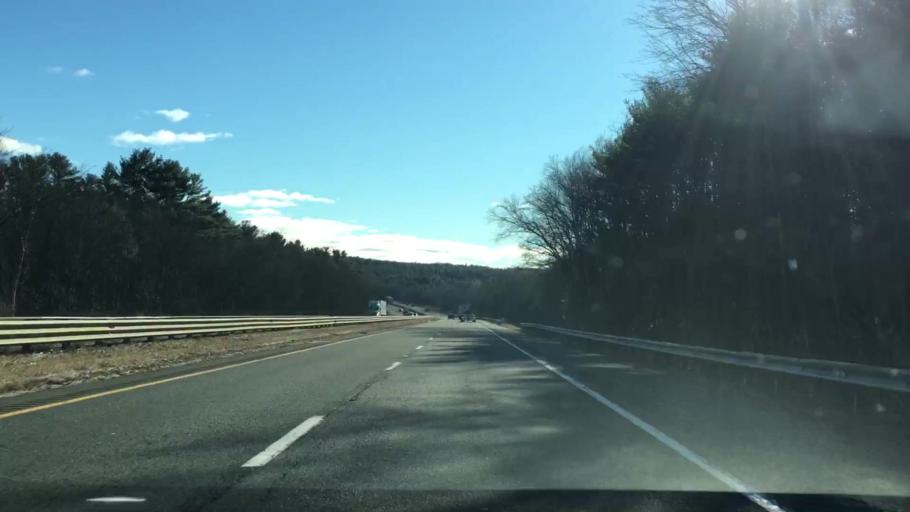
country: US
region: Massachusetts
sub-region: Worcester County
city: Fiskdale
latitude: 42.1404
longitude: -72.1352
